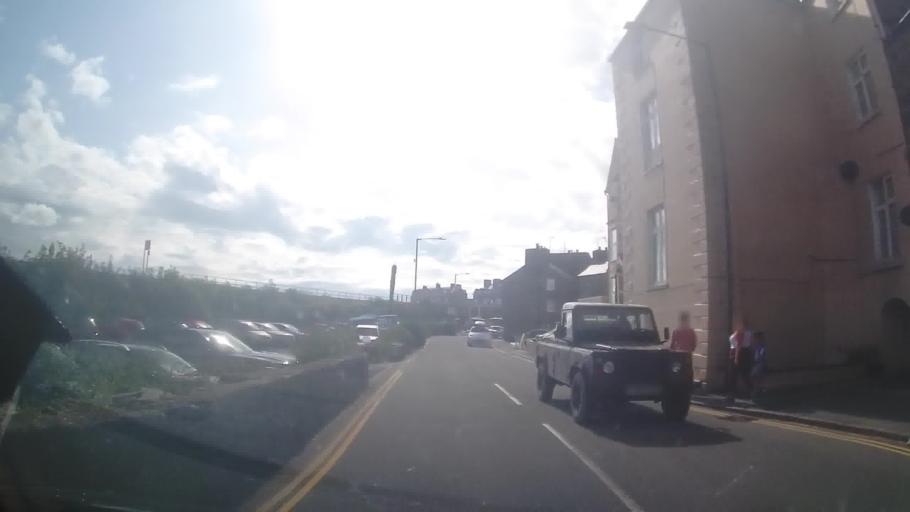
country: GB
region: Wales
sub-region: Gwynedd
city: Barmouth
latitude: 52.7202
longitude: -4.0490
